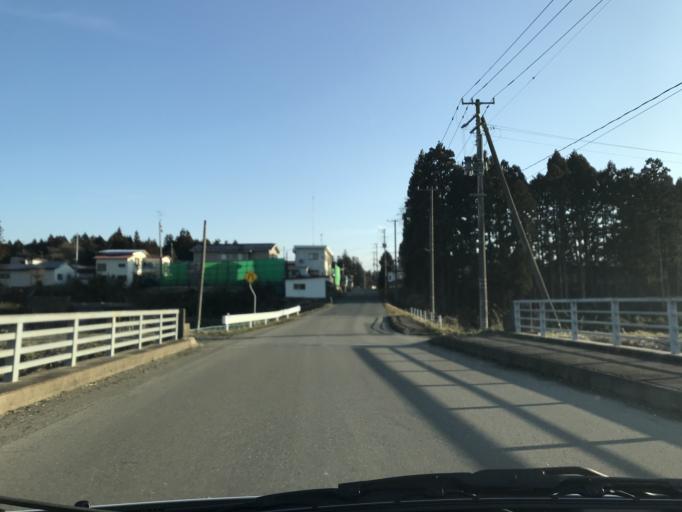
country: JP
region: Iwate
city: Mizusawa
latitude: 39.2070
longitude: 141.1181
